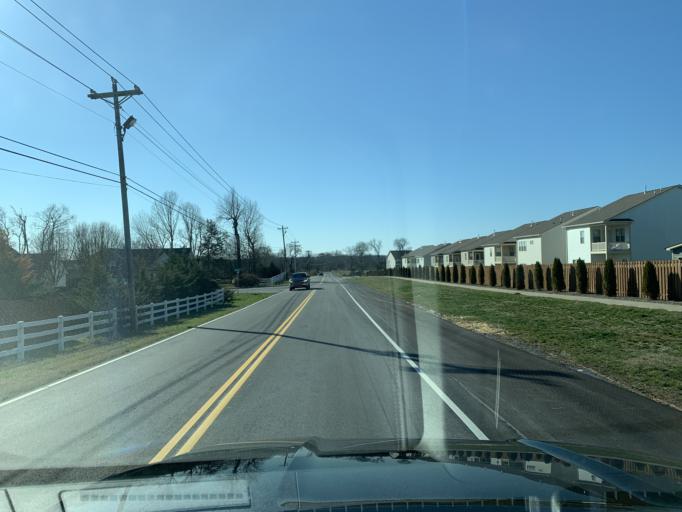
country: US
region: Tennessee
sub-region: Maury County
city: Spring Hill
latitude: 35.7499
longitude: -86.9026
